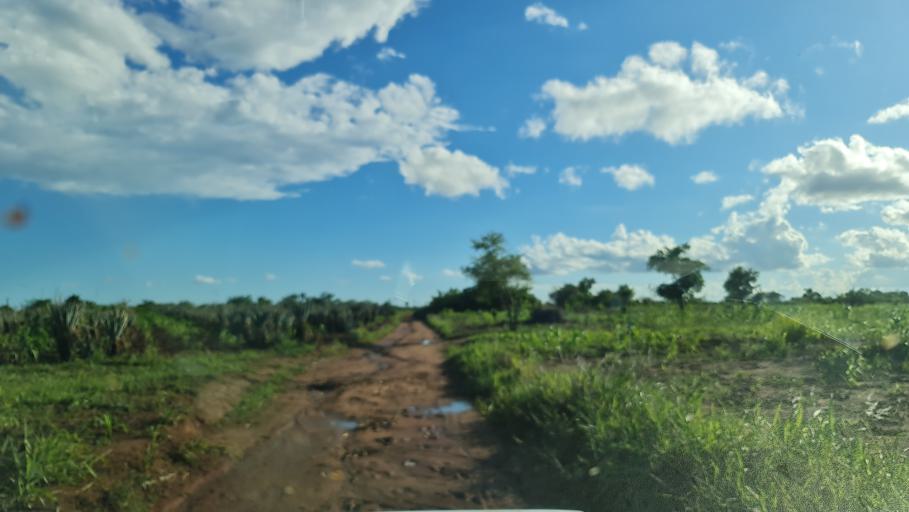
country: MZ
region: Nampula
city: Ilha de Mocambique
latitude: -14.9401
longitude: 40.2002
